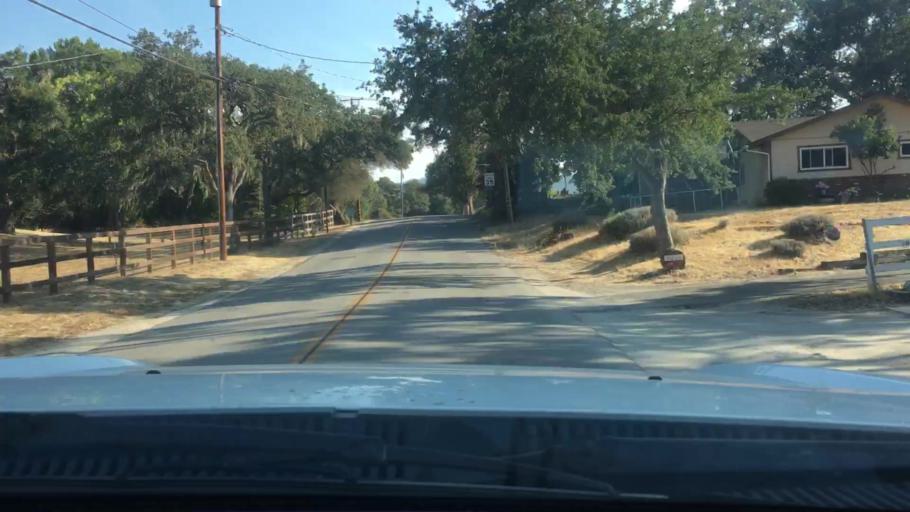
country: US
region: California
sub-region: San Luis Obispo County
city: Atascadero
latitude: 35.4587
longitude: -120.6539
